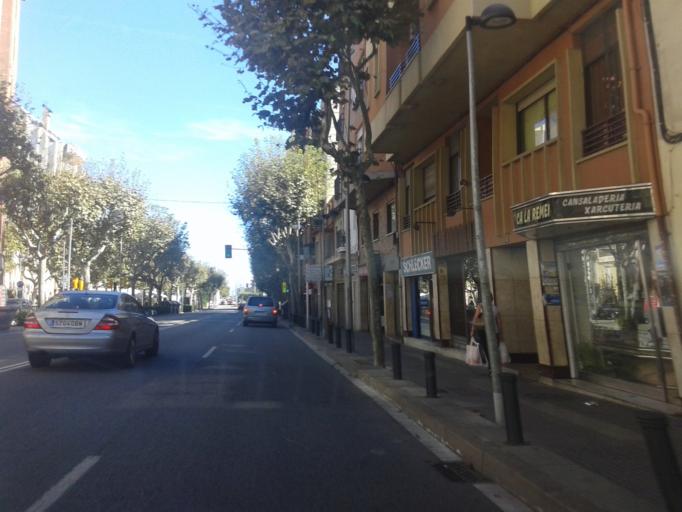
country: ES
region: Catalonia
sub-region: Provincia de Barcelona
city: Esplugues de Llobregat
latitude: 41.3776
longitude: 2.0869
